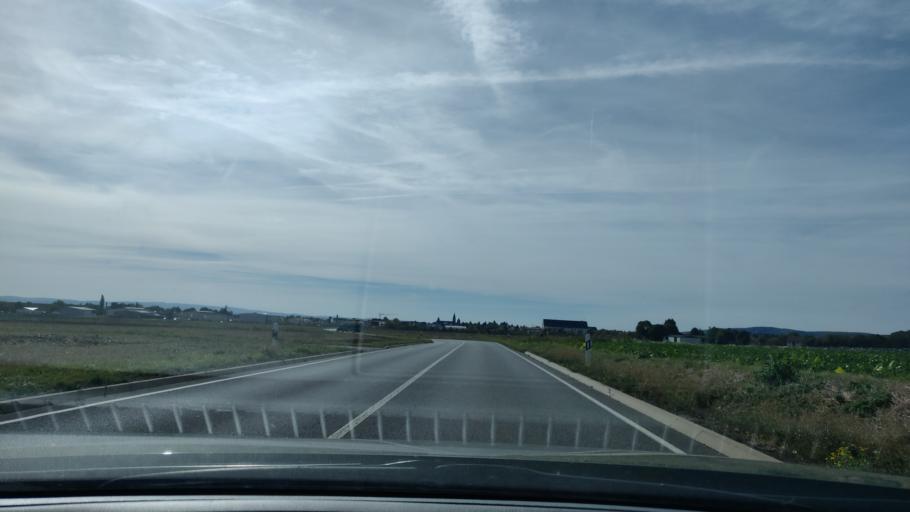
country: DE
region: Hesse
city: Fritzlar
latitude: 51.1474
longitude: 9.2729
